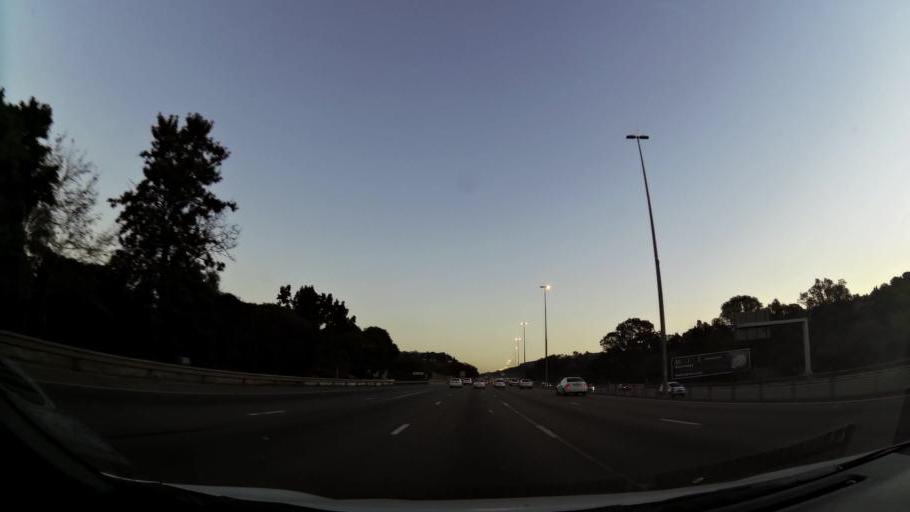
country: ZA
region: Gauteng
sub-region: City of Tshwane Metropolitan Municipality
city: Pretoria
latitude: -25.7932
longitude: 28.2674
